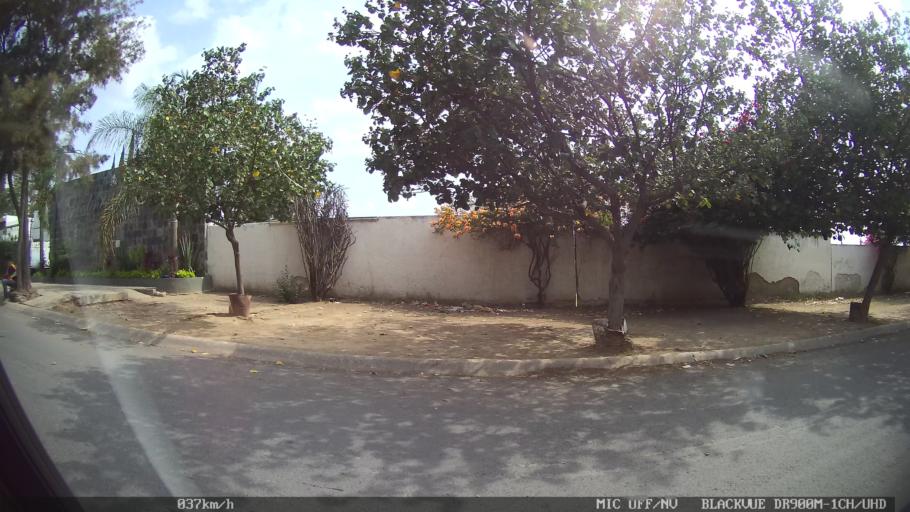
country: MX
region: Jalisco
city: Coyula
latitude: 20.6521
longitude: -103.2189
